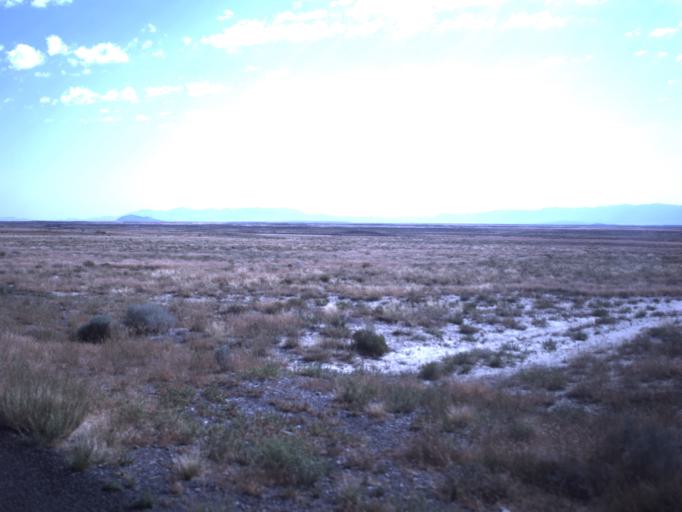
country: US
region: Utah
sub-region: Beaver County
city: Milford
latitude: 38.8597
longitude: -112.8391
